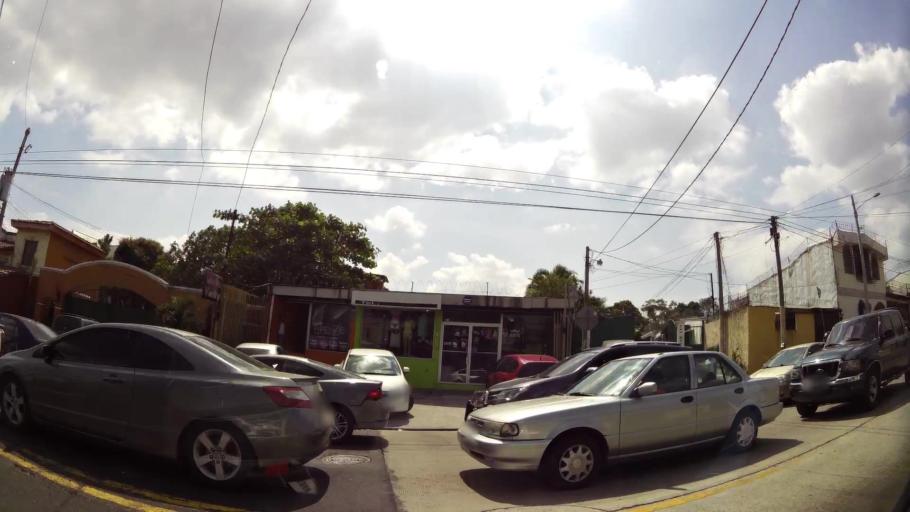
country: SV
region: San Salvador
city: Mejicanos
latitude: 13.7106
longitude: -89.2337
